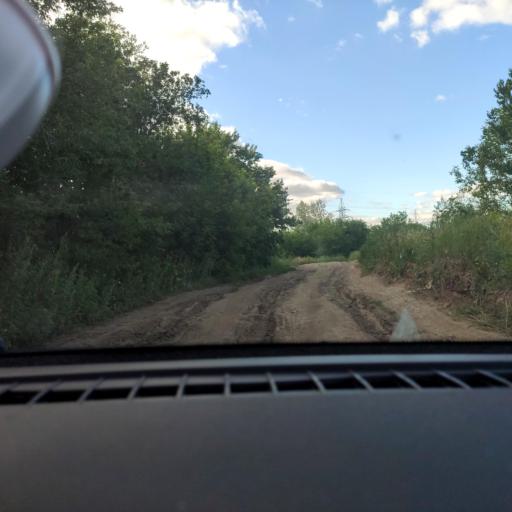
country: RU
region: Samara
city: Samara
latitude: 53.1782
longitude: 50.2371
